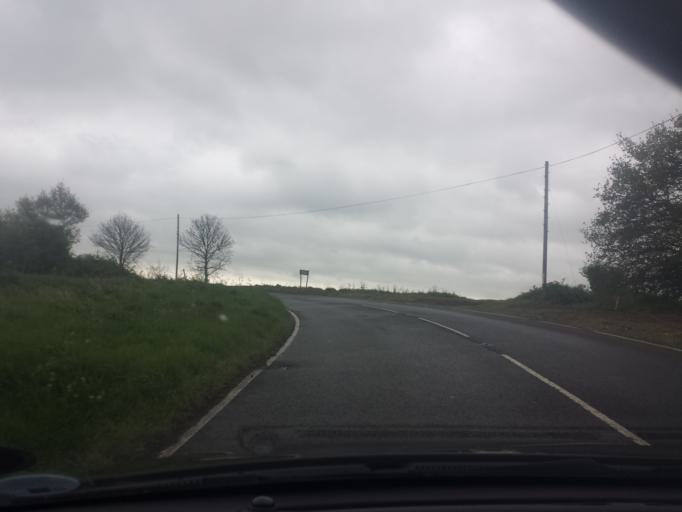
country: GB
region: England
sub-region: Essex
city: Mistley
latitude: 51.9302
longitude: 1.1384
